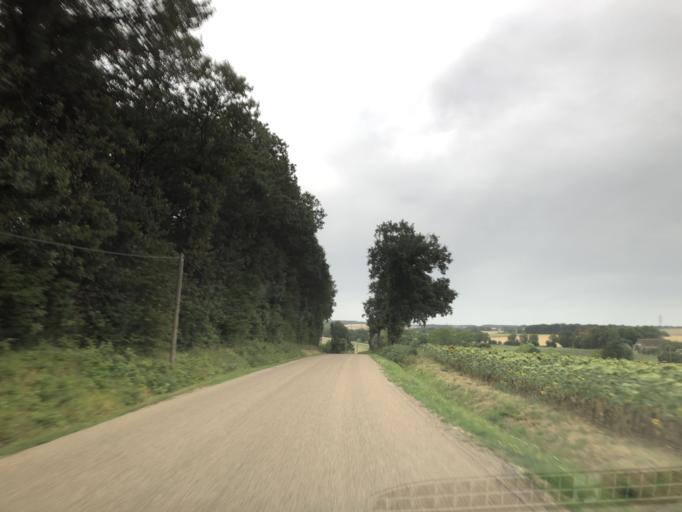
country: FR
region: Bourgogne
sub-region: Departement de l'Yonne
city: Charny
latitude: 47.9573
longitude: 3.1376
